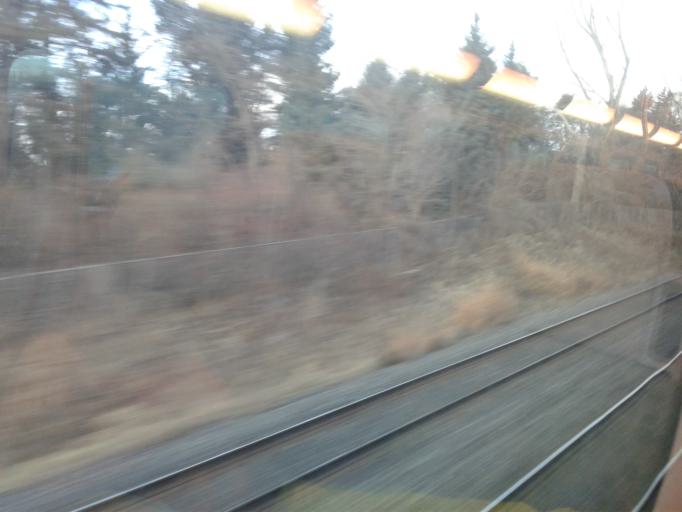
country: CA
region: Ontario
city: Mississauga
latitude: 43.5386
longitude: -79.6062
